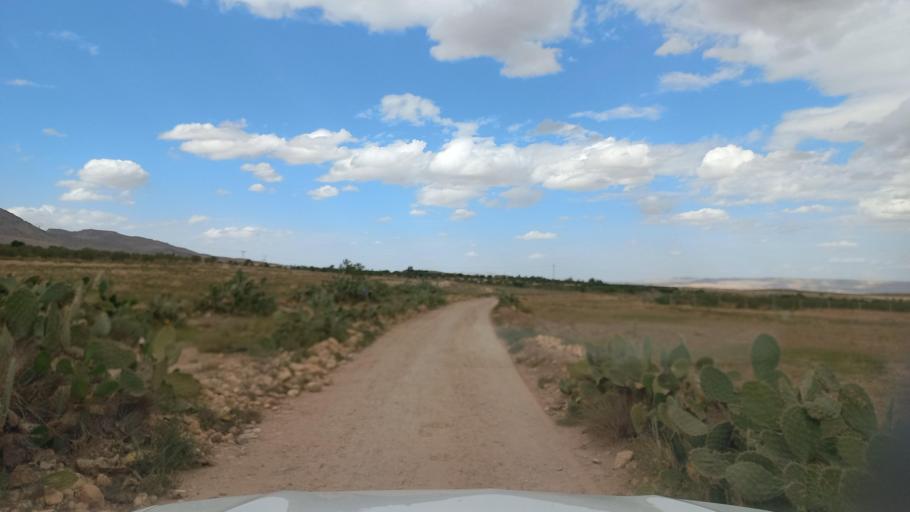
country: TN
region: Al Qasrayn
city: Sbiba
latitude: 35.4344
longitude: 9.0977
